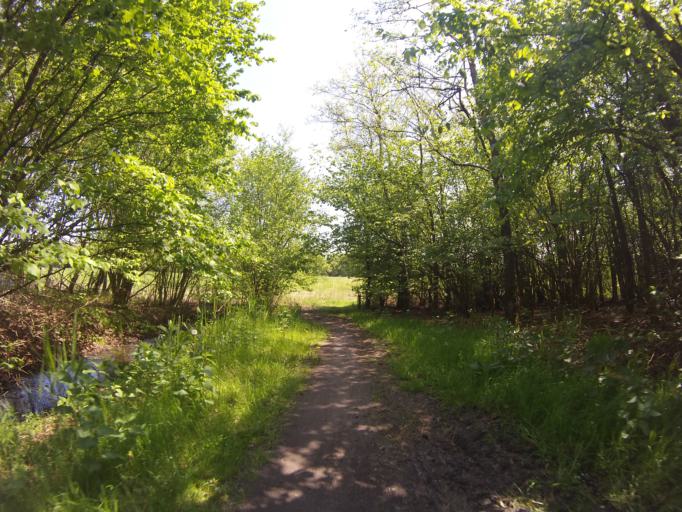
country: NL
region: Flevoland
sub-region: Gemeente Zeewolde
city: Zeewolde
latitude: 52.2940
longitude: 5.5349
